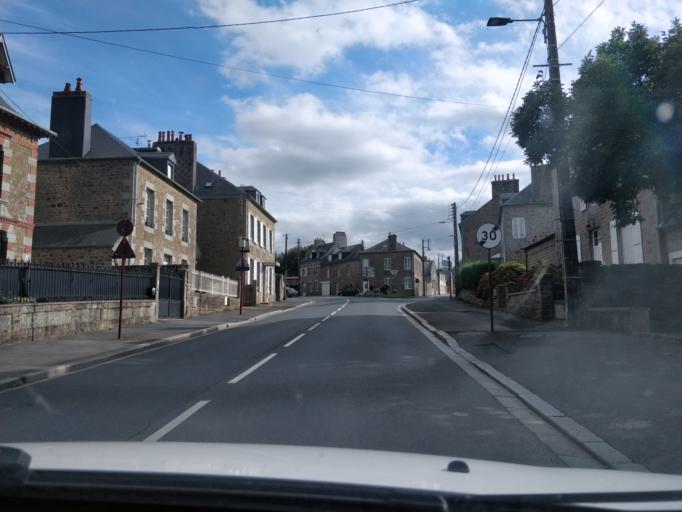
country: FR
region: Lower Normandy
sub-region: Departement du Calvados
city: Vire
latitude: 48.8410
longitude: -0.8961
